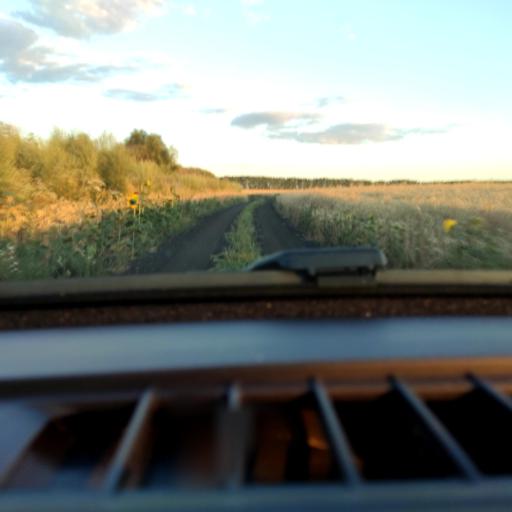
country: RU
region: Voronezj
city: Verkhnyaya Khava
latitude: 51.5850
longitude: 39.8711
